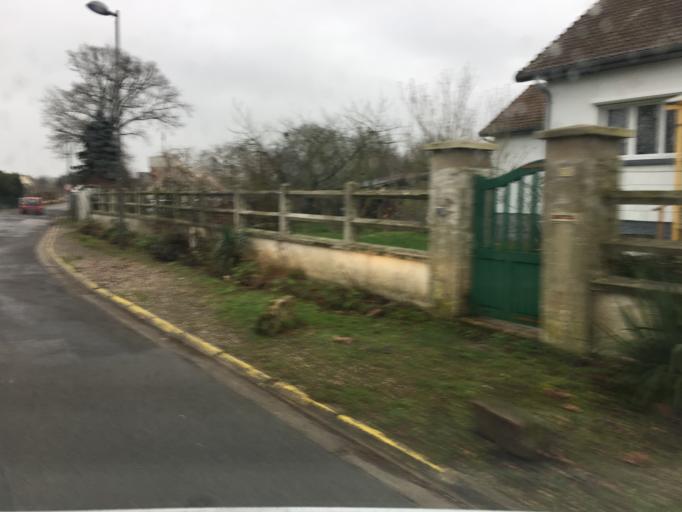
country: FR
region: Picardie
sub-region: Departement de la Somme
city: Saint-Valery-sur-Somme
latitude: 50.1822
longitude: 1.6290
